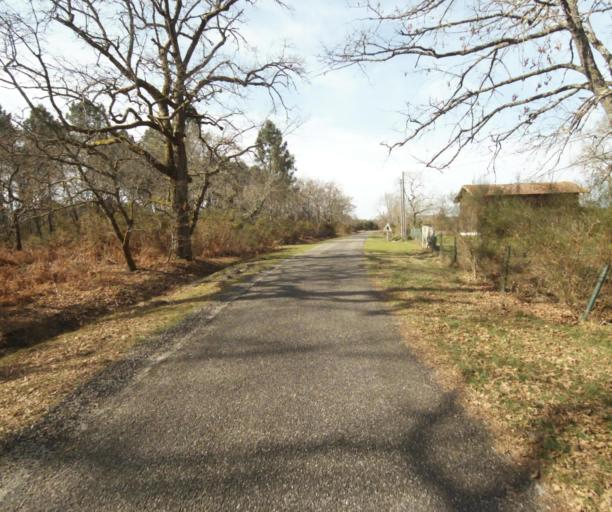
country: FR
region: Aquitaine
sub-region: Departement des Landes
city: Roquefort
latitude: 44.1361
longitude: -0.1991
